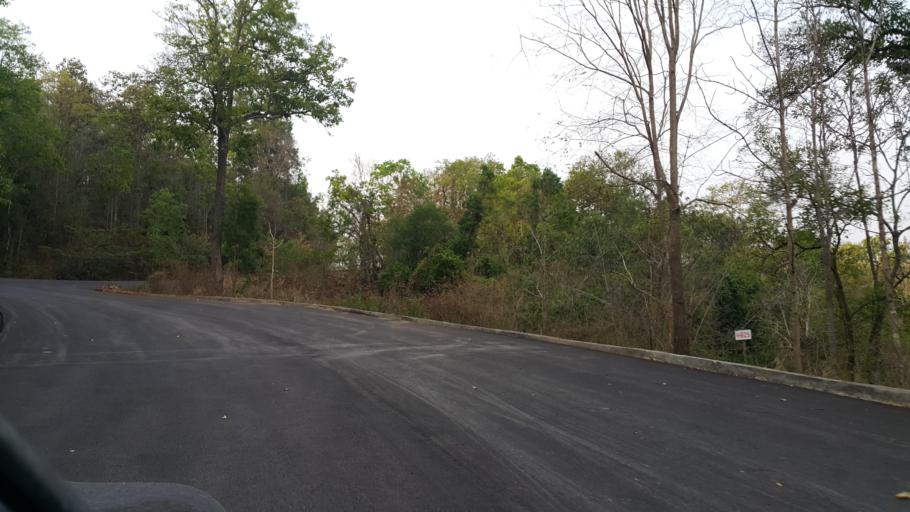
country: TH
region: Chiang Mai
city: Mae On
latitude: 18.7577
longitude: 99.2954
